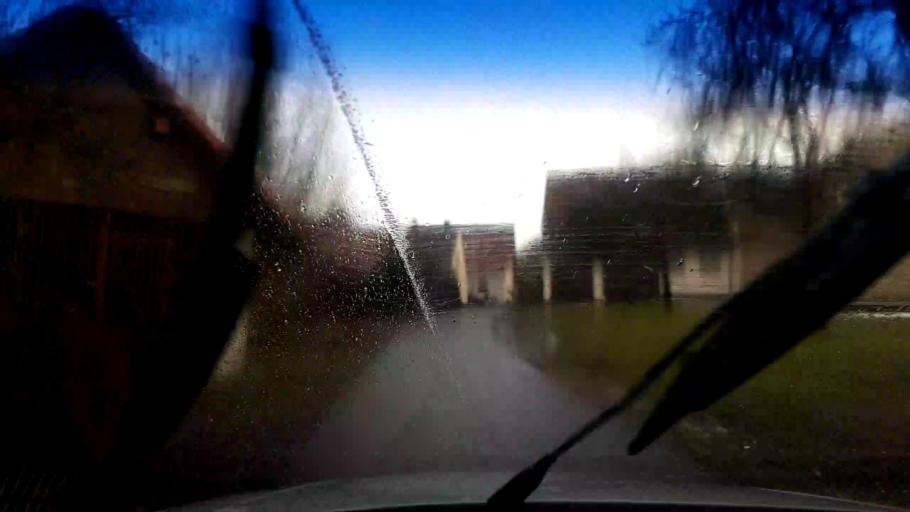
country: DE
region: Bavaria
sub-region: Upper Franconia
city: Zapfendorf
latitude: 49.9904
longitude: 10.9512
